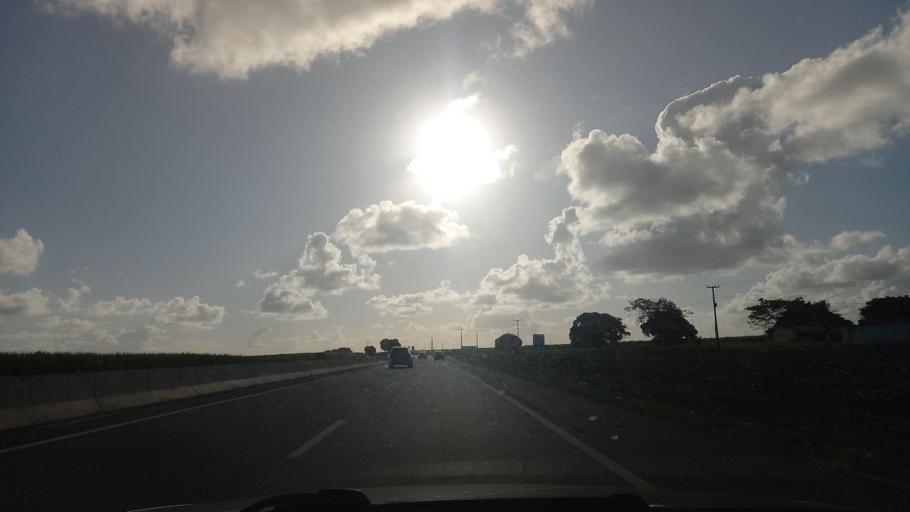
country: BR
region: Alagoas
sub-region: Sao Miguel Dos Campos
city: Sao Miguel dos Campos
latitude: -9.8069
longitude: -36.1192
